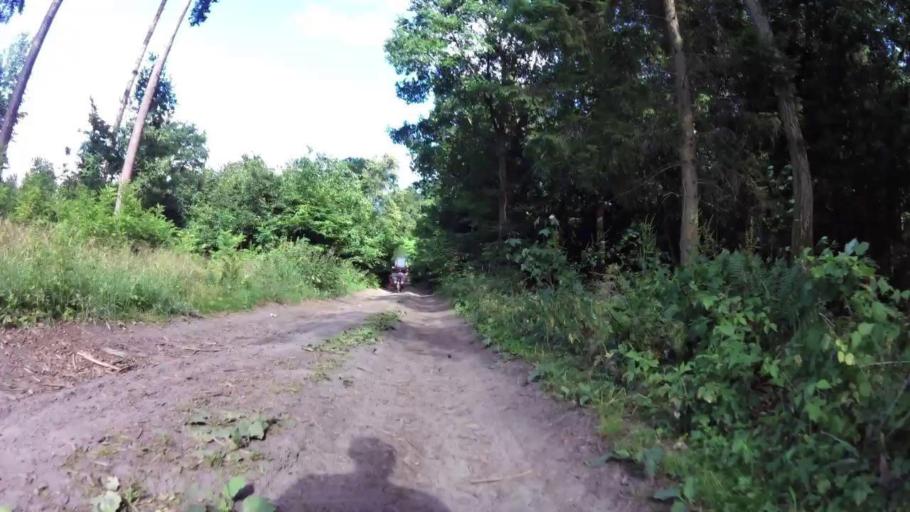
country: PL
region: West Pomeranian Voivodeship
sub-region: Powiat lobeski
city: Lobez
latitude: 53.6731
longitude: 15.7141
